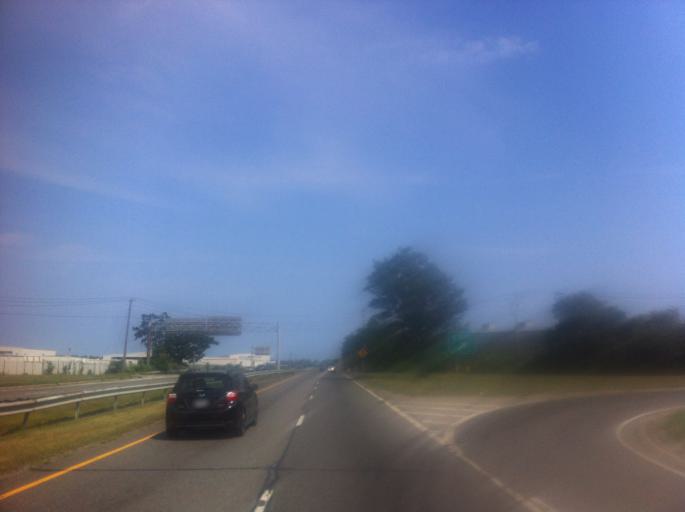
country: US
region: New York
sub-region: Suffolk County
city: East Farmingdale
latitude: 40.7225
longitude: -73.4248
